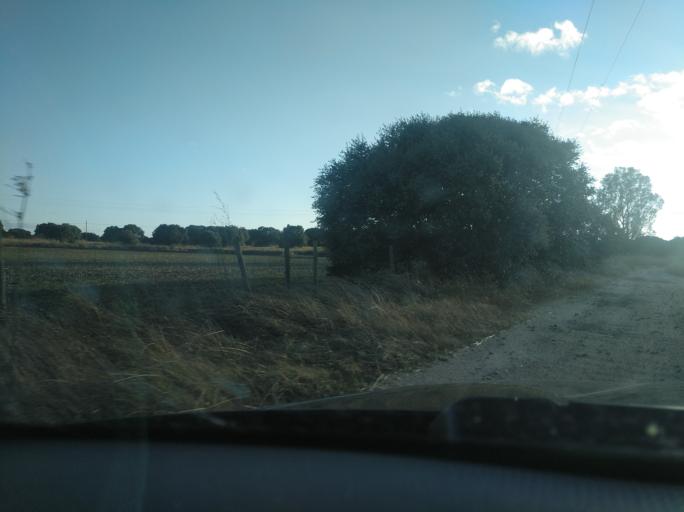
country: PT
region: Portalegre
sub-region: Campo Maior
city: Campo Maior
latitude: 39.0359
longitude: -6.9847
